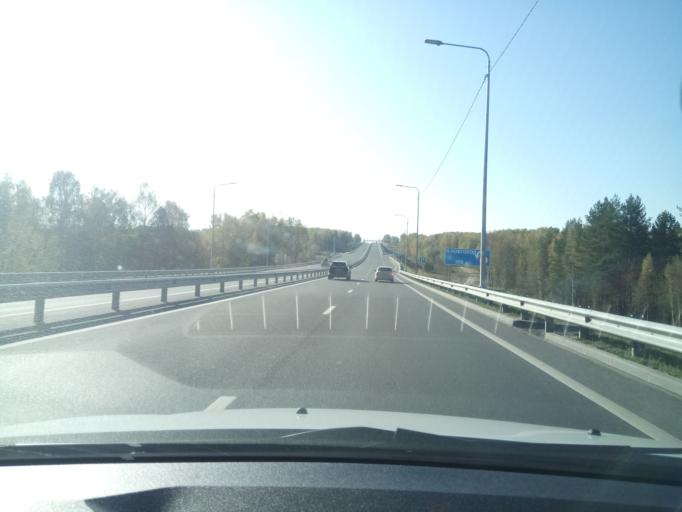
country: RU
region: Nizjnij Novgorod
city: Burevestnik
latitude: 56.0099
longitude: 43.9659
